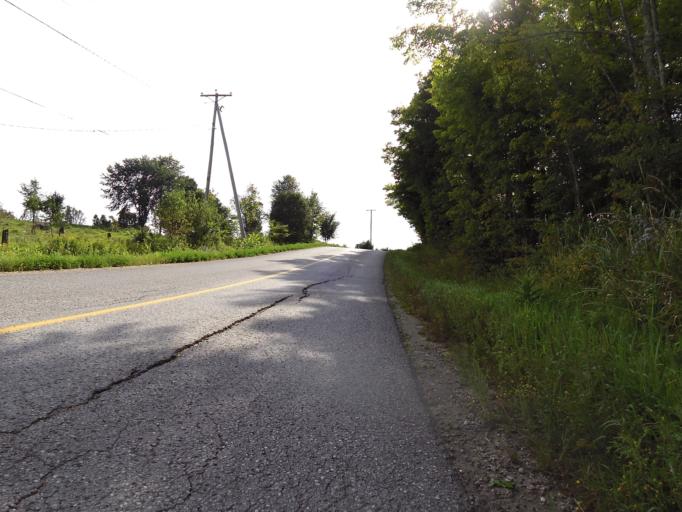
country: CA
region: Quebec
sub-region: Outaouais
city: Wakefield
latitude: 45.6841
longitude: -75.9978
